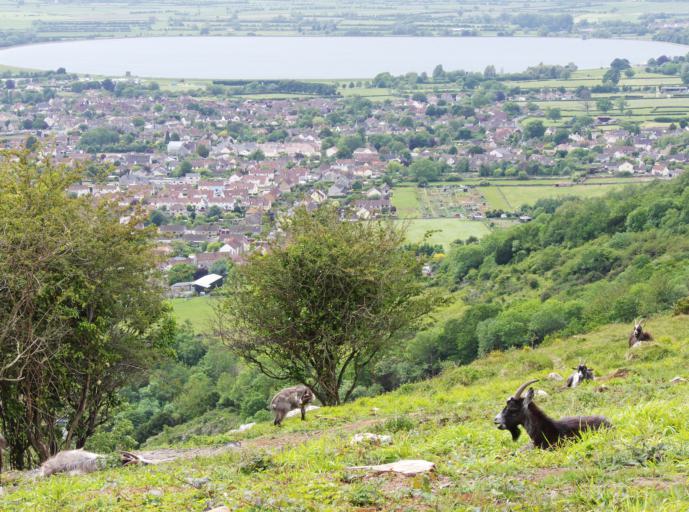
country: GB
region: England
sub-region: Somerset
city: Bradley Cross
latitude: 51.2845
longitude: -2.7584
